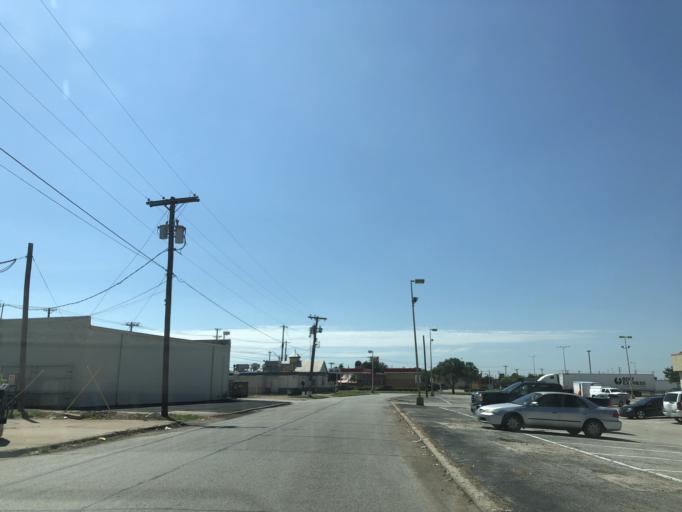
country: US
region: Texas
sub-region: Dallas County
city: Sunnyvale
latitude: 32.8472
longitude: -96.5971
